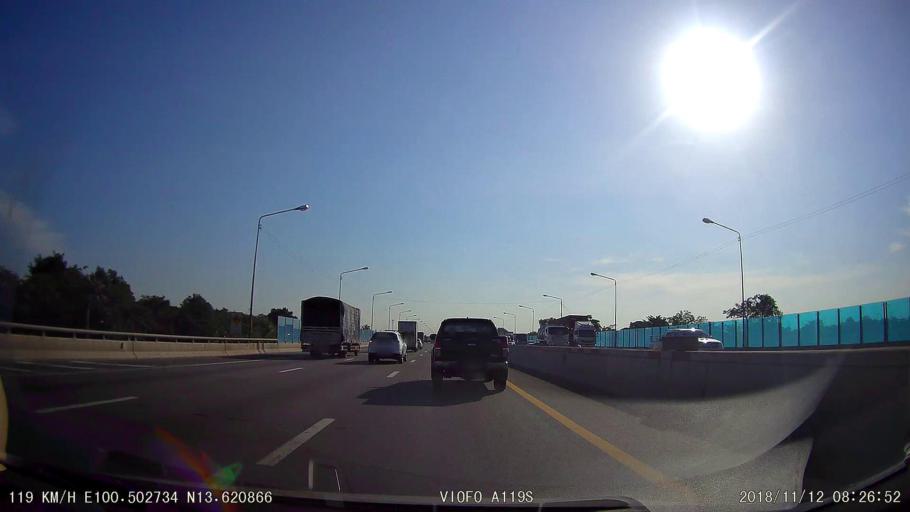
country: TH
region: Bangkok
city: Thung Khru
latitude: 13.6209
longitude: 100.5033
